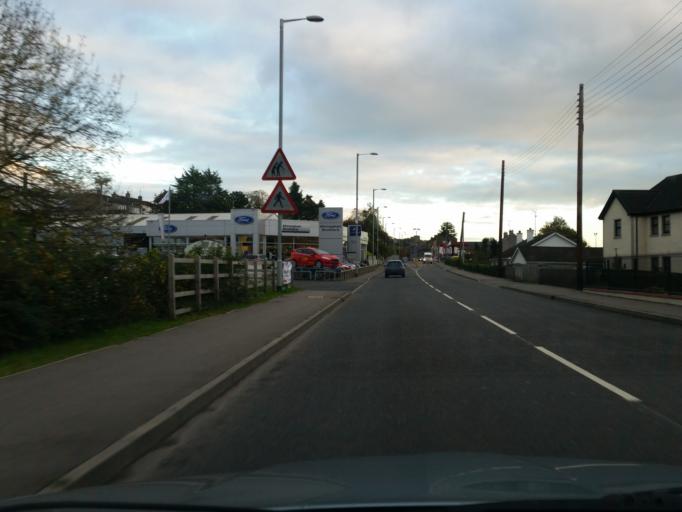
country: GB
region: Northern Ireland
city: Lisnaskea
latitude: 54.2573
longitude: -7.4500
